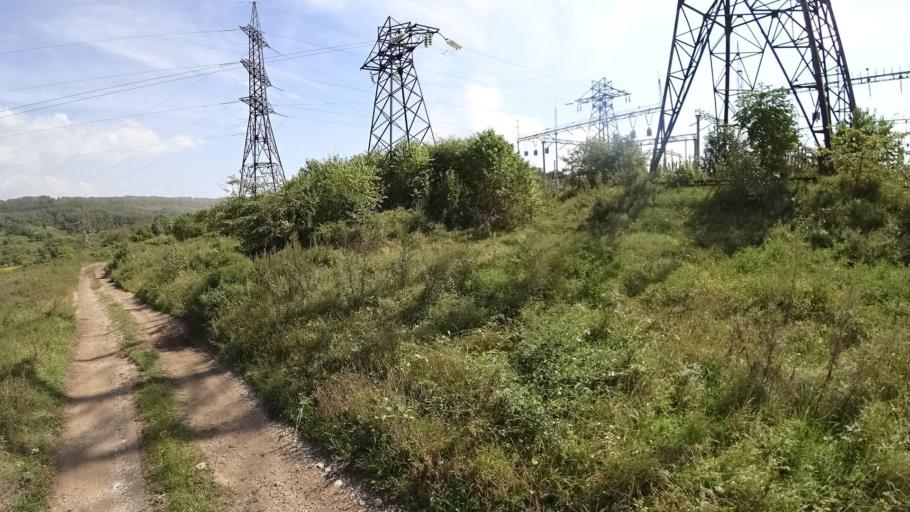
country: RU
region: Jewish Autonomous Oblast
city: Londoko
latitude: 49.0150
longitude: 131.8969
